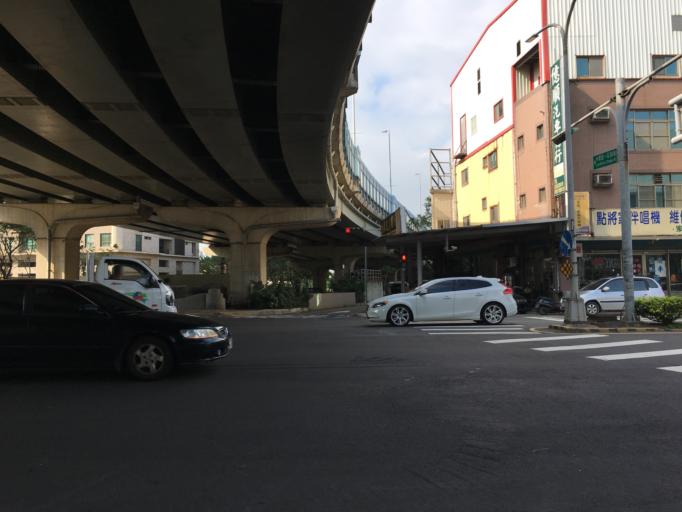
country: TW
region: Taiwan
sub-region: Hsinchu
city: Hsinchu
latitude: 24.8109
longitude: 120.9866
